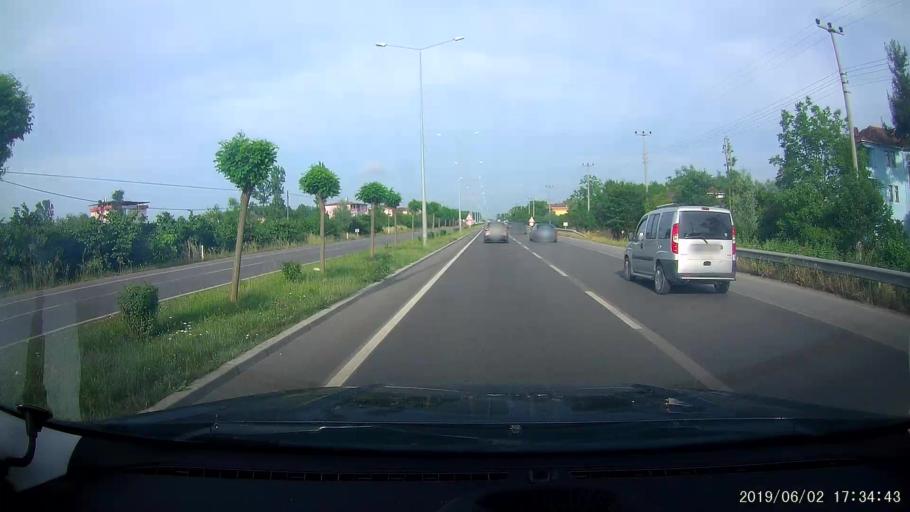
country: TR
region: Samsun
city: Terme
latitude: 41.2200
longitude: 36.8740
